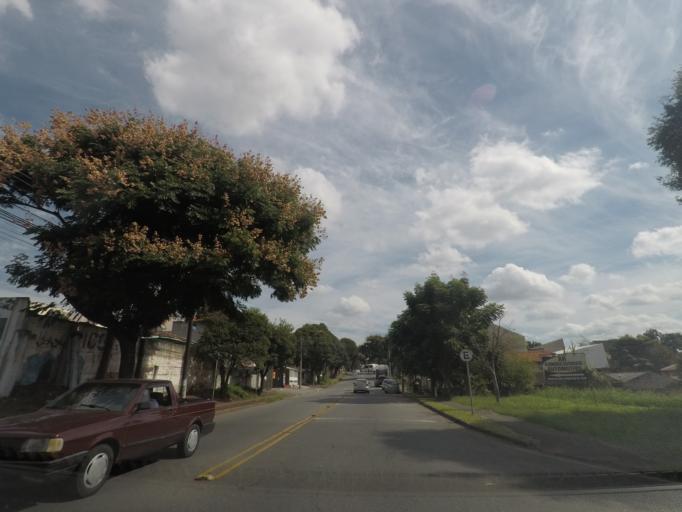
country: BR
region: Parana
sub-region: Sao Jose Dos Pinhais
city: Sao Jose dos Pinhais
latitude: -25.4929
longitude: -49.2606
